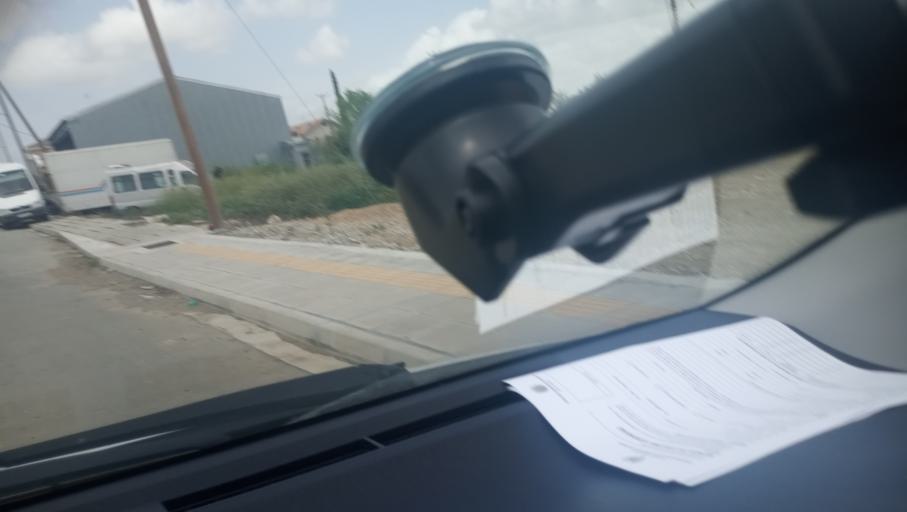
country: CY
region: Lefkosia
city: Pano Deftera
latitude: 35.0739
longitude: 33.2660
